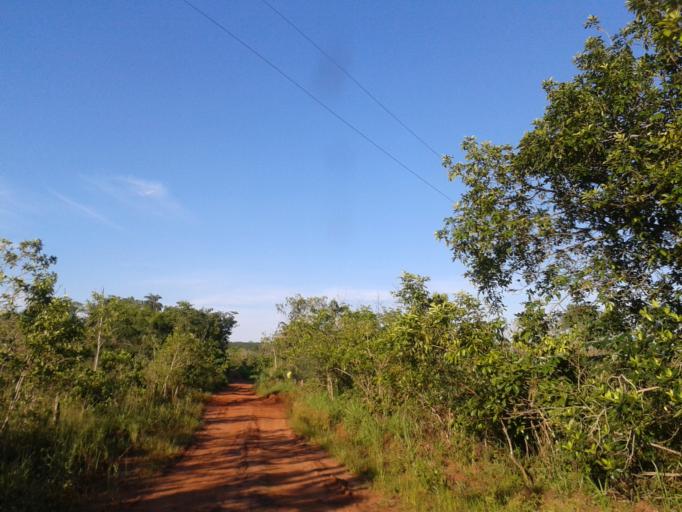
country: BR
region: Minas Gerais
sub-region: Santa Vitoria
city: Santa Vitoria
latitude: -18.9617
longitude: -49.8683
